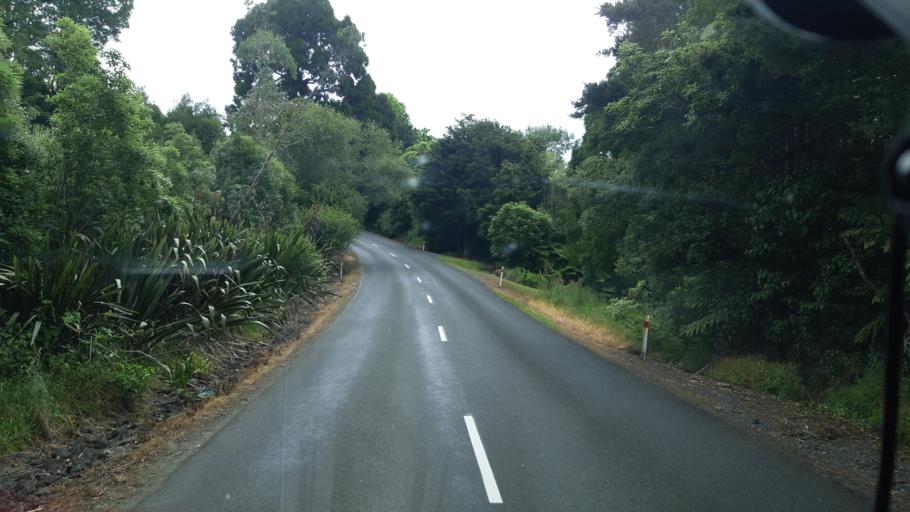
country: NZ
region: Waikato
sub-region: Waikato District
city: Raglan
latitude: -37.8447
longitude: 175.0292
